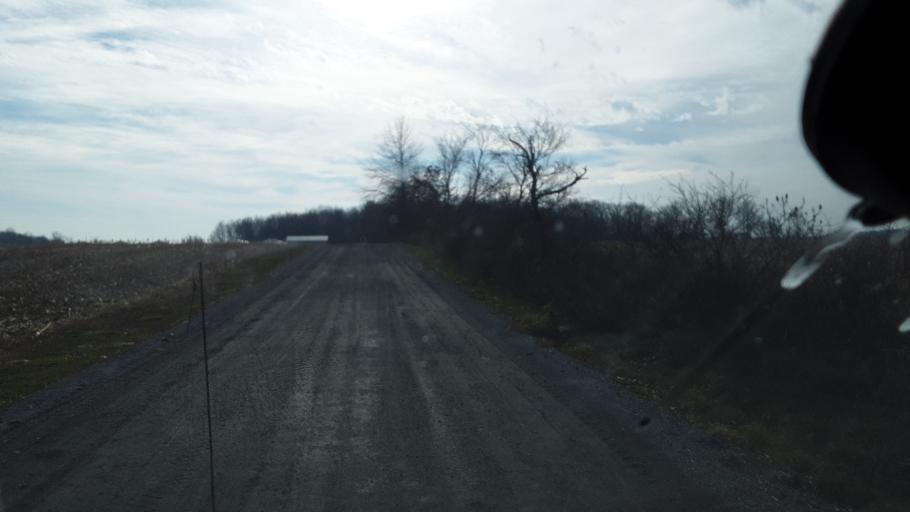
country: US
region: Ohio
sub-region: Defiance County
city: Hicksville
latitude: 41.3525
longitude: -84.7814
